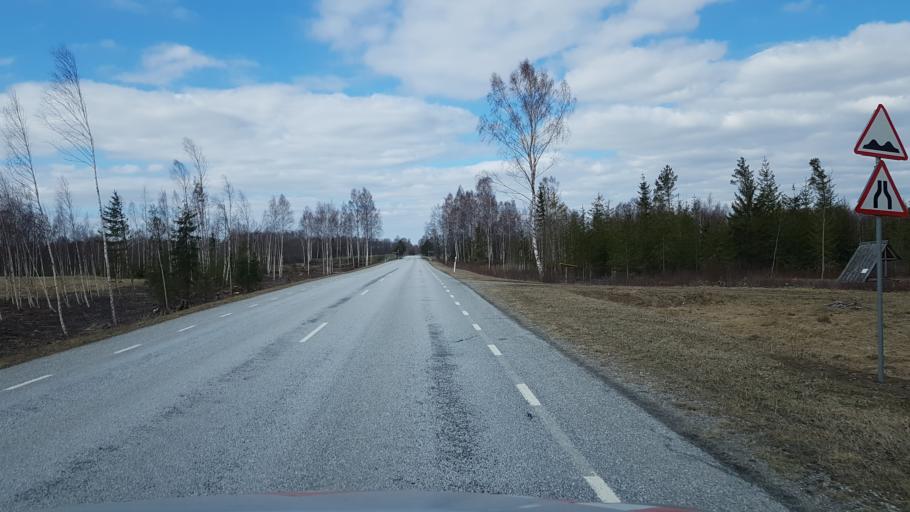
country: EE
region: Laeaene-Virumaa
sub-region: Rakke vald
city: Rakke
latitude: 58.9392
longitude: 26.2034
